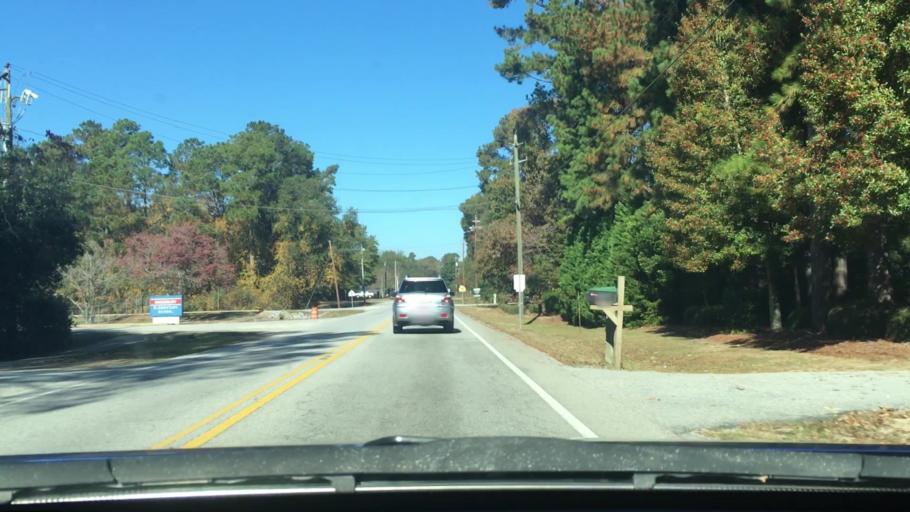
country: US
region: South Carolina
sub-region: Sumter County
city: South Sumter
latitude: 33.8906
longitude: -80.3664
